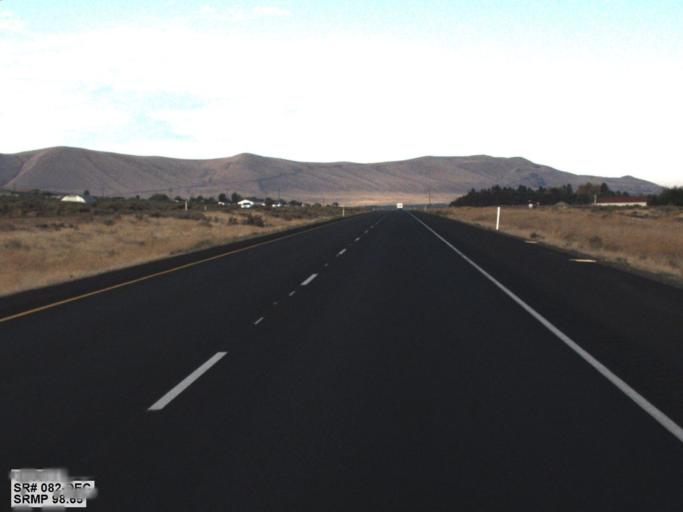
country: US
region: Washington
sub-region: Benton County
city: Benton City
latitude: 46.2586
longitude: -119.4341
